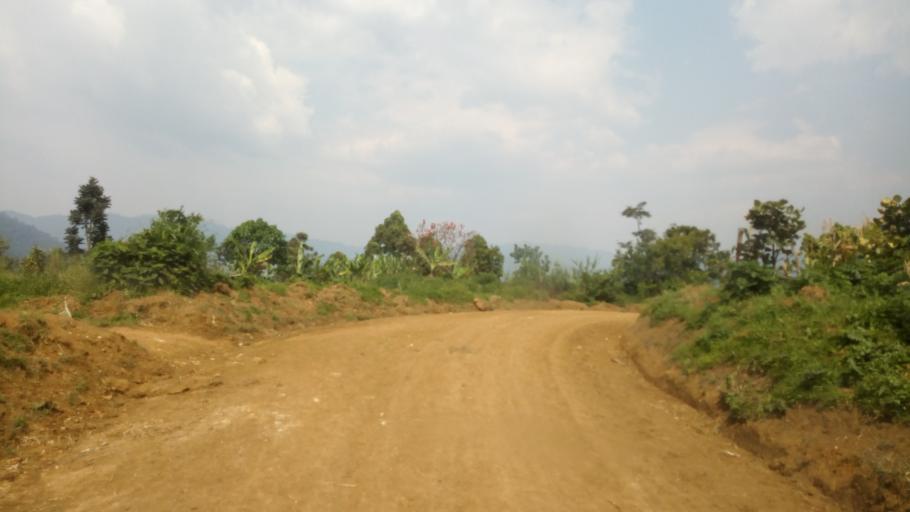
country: UG
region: Western Region
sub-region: Kanungu District
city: Ntungamo
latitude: -1.0213
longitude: 29.5864
